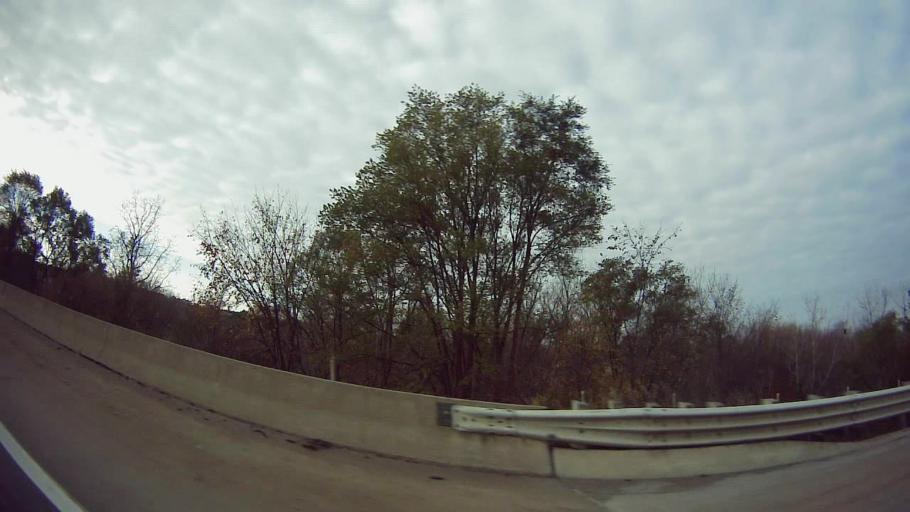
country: US
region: Michigan
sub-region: Monroe County
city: Carleton
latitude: 42.0809
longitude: -83.3742
